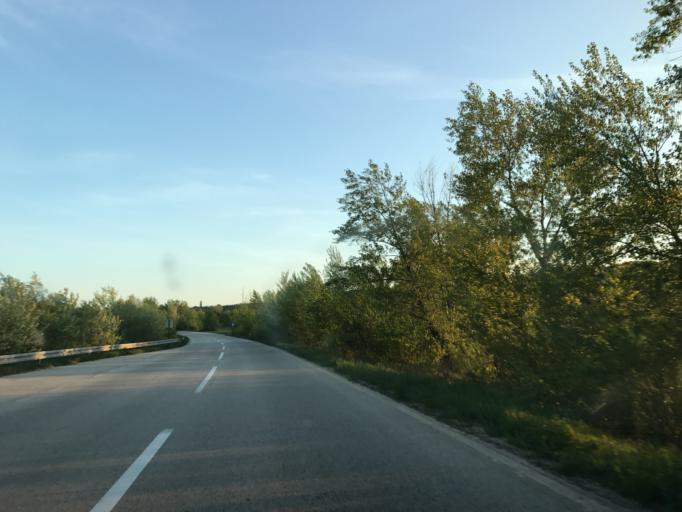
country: RO
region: Mehedinti
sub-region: Comuna Gogosu
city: Ostrovu Mare
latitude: 44.3975
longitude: 22.4649
